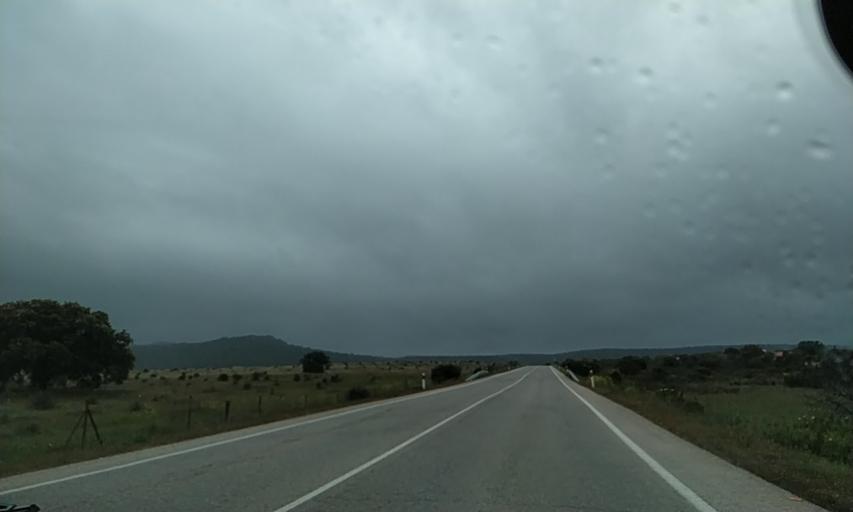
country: ES
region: Extremadura
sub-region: Provincia de Caceres
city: Malpartida de Caceres
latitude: 39.3216
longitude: -6.4992
